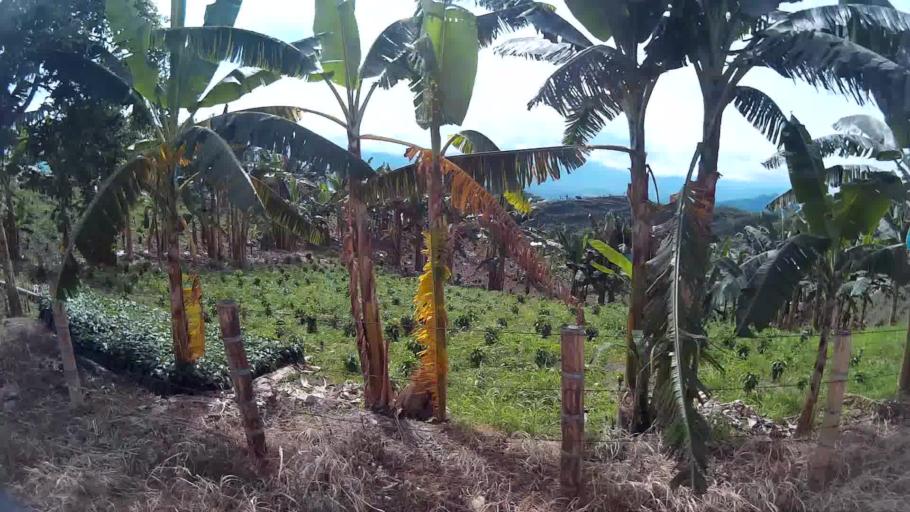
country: CO
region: Caldas
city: Belalcazar
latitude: 4.9683
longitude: -75.8226
